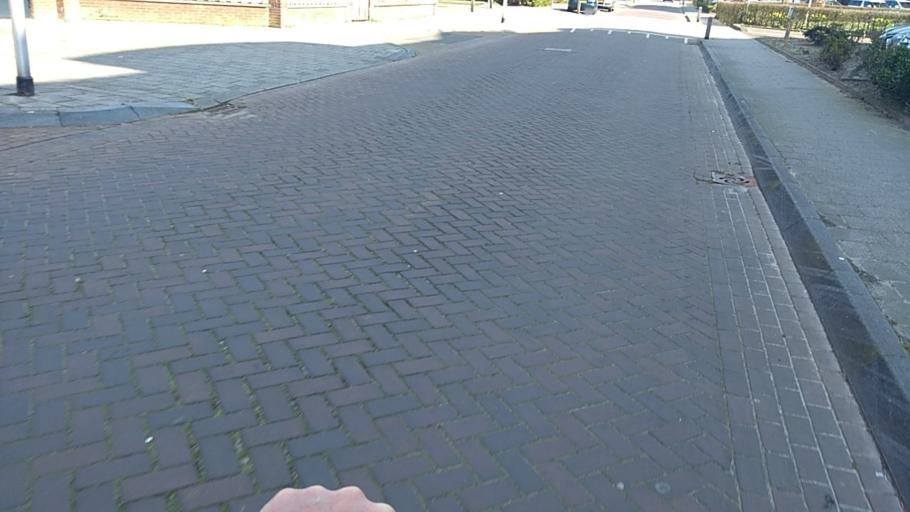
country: NL
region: Overijssel
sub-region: Gemeente Almelo
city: Almelo
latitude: 52.3413
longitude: 6.6743
